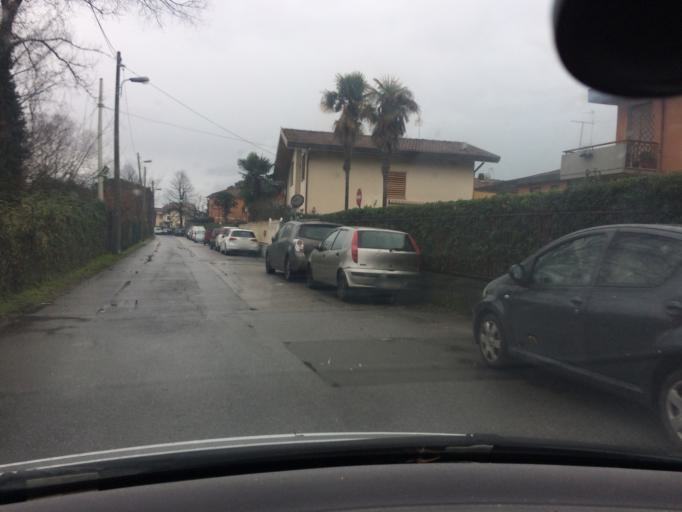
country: IT
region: Tuscany
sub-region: Provincia di Massa-Carrara
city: Massa
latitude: 44.0171
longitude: 10.0928
